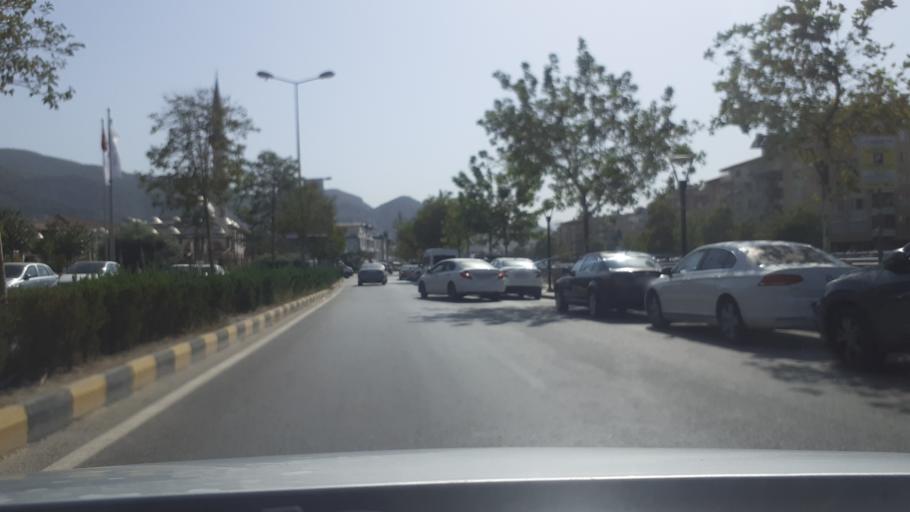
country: TR
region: Hatay
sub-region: Antakya Ilcesi
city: Antakya
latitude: 36.2086
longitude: 36.1623
